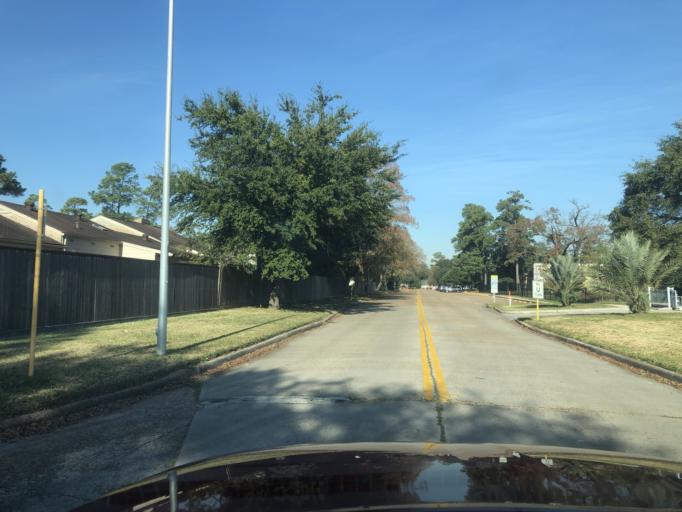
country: US
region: Texas
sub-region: Harris County
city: Spring
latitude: 30.0138
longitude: -95.4582
